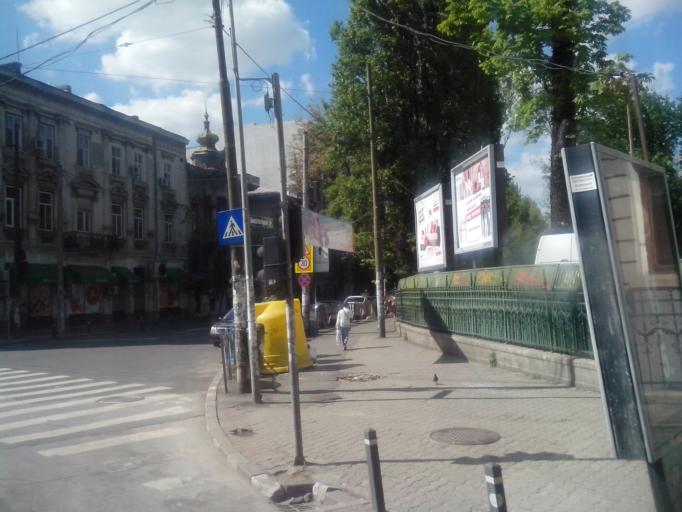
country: RO
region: Bucuresti
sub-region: Municipiul Bucuresti
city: Bucuresti
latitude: 44.4348
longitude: 26.0900
